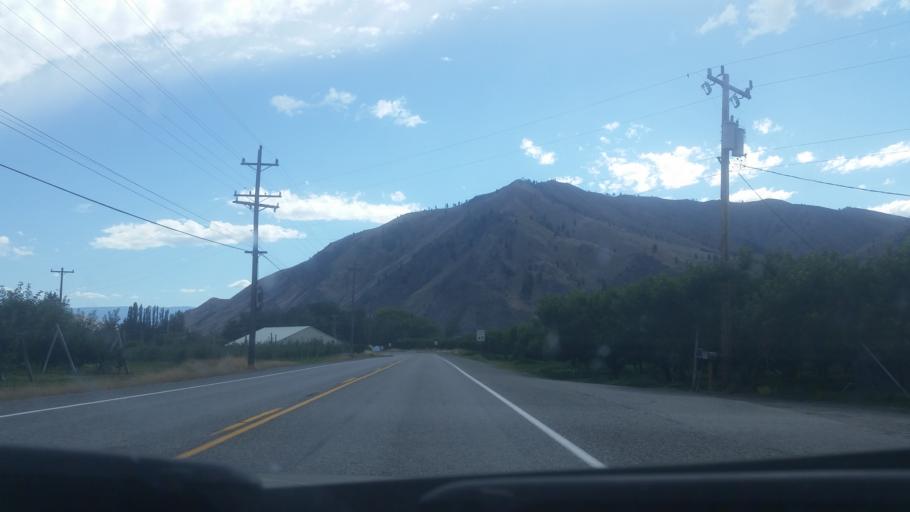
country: US
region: Washington
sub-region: Chelan County
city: Entiat
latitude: 47.6327
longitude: -120.2253
